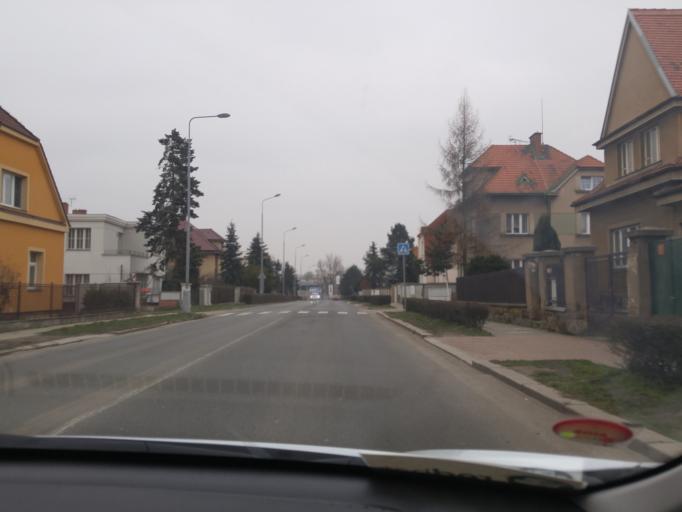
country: CZ
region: Central Bohemia
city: Brandys nad Labem-Stara Boleslav
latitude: 50.1820
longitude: 14.6666
